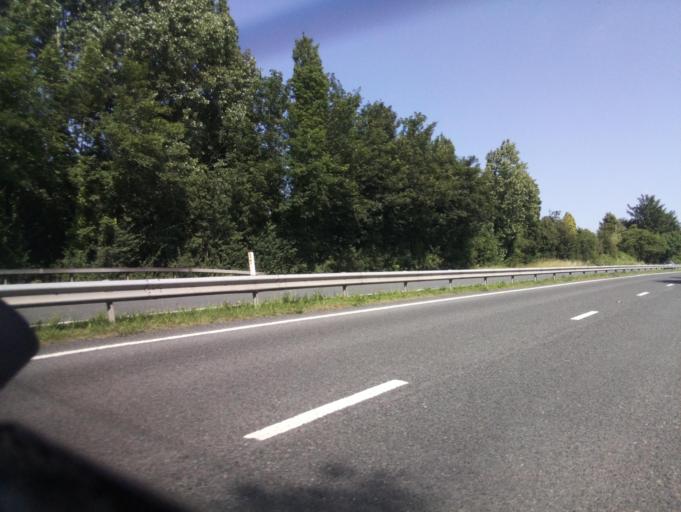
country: GB
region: England
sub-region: Worcestershire
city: Barnt Green
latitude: 52.3291
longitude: -2.0189
